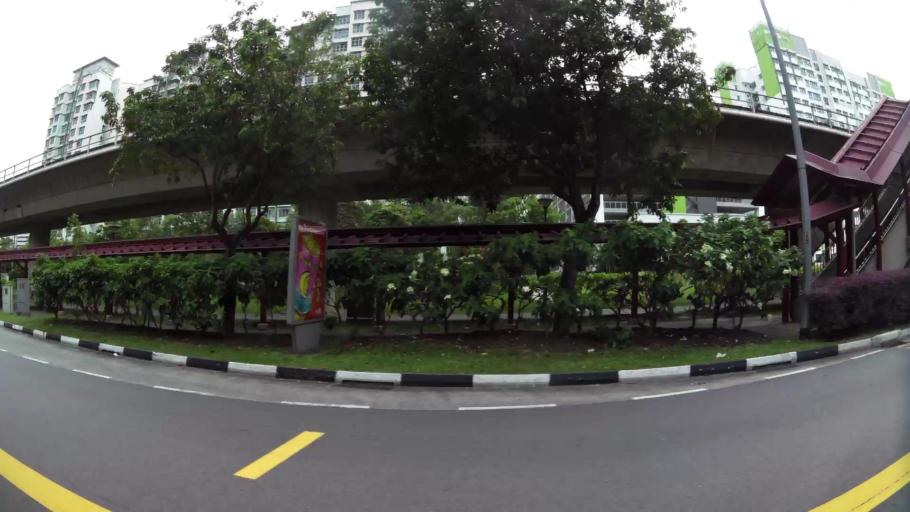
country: MY
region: Johor
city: Johor Bahru
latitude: 1.4390
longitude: 103.7938
